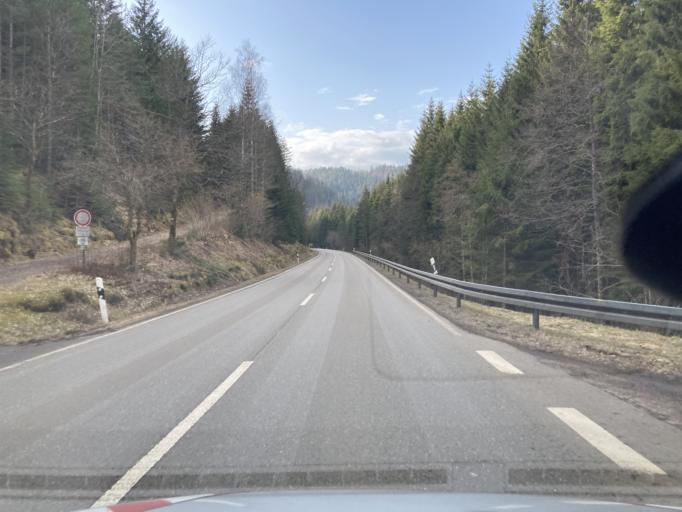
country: DE
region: Baden-Wuerttemberg
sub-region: Karlsruhe Region
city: Neuweiler
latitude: 48.6865
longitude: 8.5741
